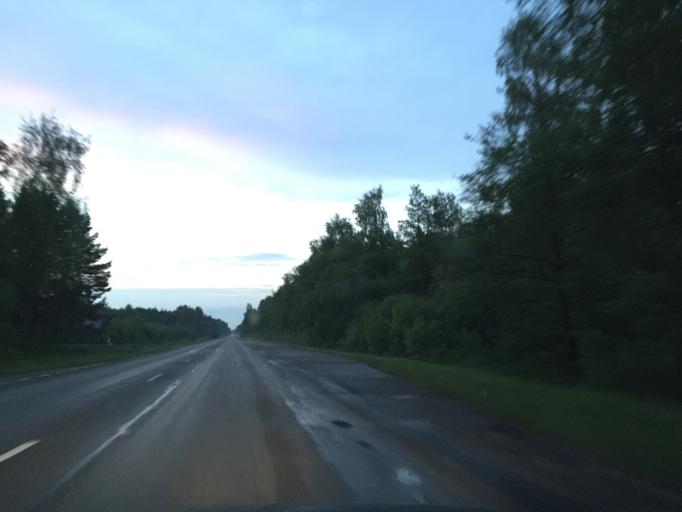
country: LT
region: Klaipedos apskritis
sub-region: Klaipeda
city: Palanga
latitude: 55.8959
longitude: 21.0661
